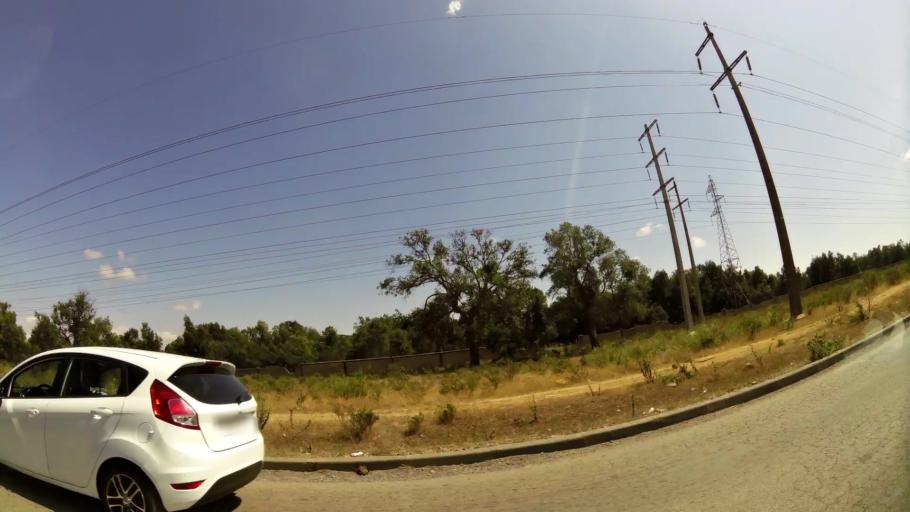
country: MA
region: Gharb-Chrarda-Beni Hssen
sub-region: Kenitra Province
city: Kenitra
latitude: 34.2368
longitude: -6.5636
